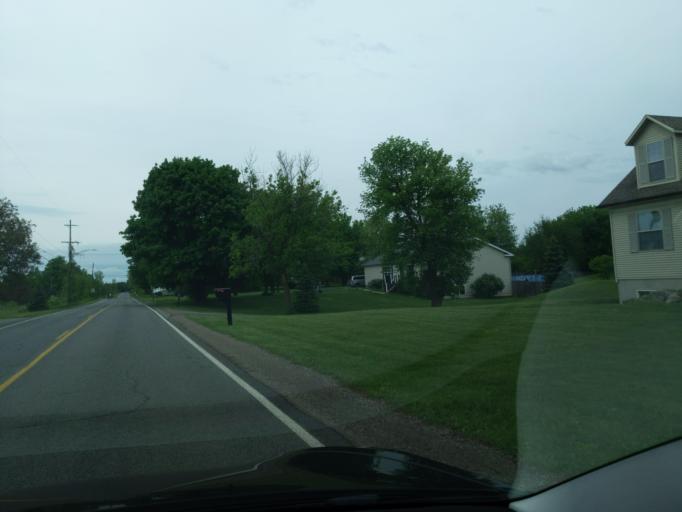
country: US
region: Michigan
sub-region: Ingham County
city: Mason
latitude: 42.5263
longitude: -84.4281
